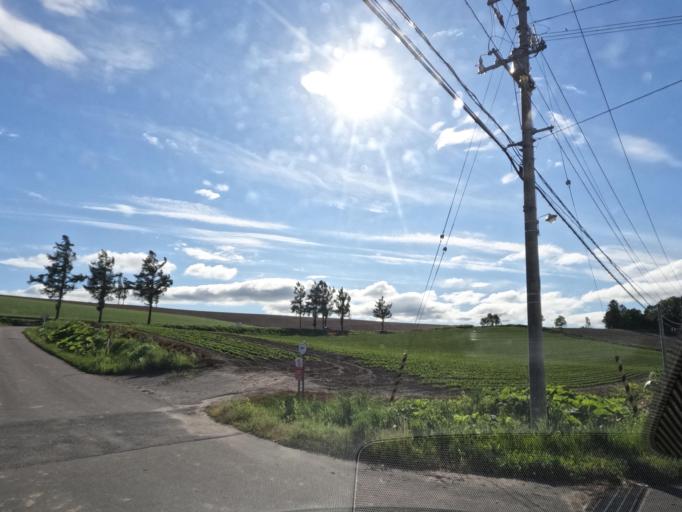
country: JP
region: Hokkaido
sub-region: Asahikawa-shi
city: Asahikawa
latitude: 43.5982
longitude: 142.4304
